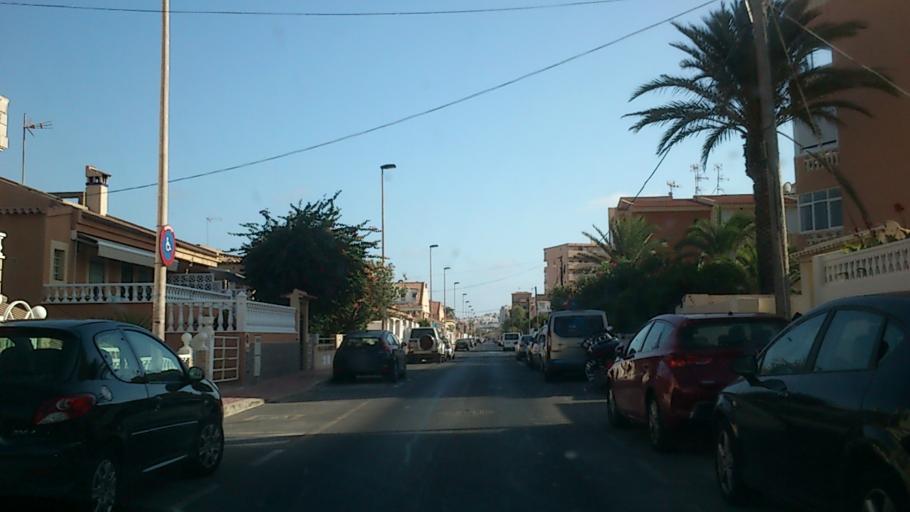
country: ES
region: Valencia
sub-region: Provincia de Alicante
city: Torrevieja
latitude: 38.0233
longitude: -0.6550
